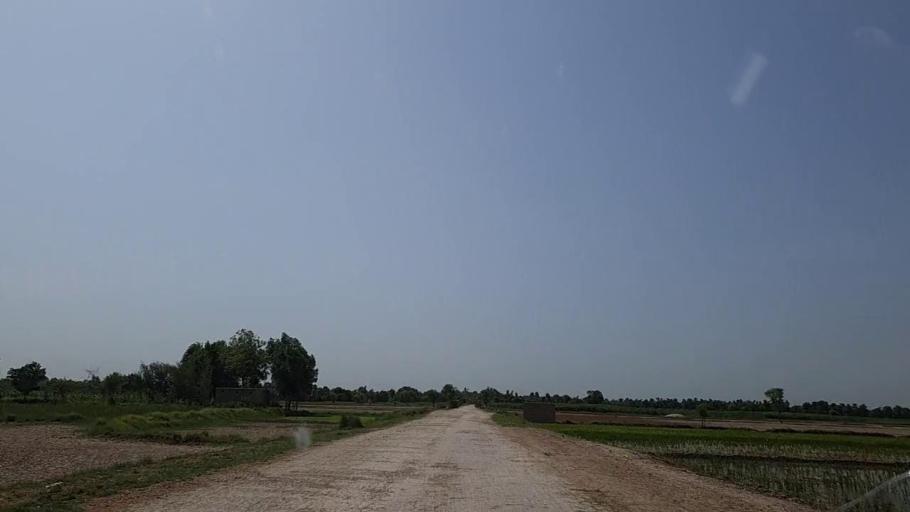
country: PK
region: Sindh
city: Naushahro Firoz
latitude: 26.8365
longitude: 68.0177
